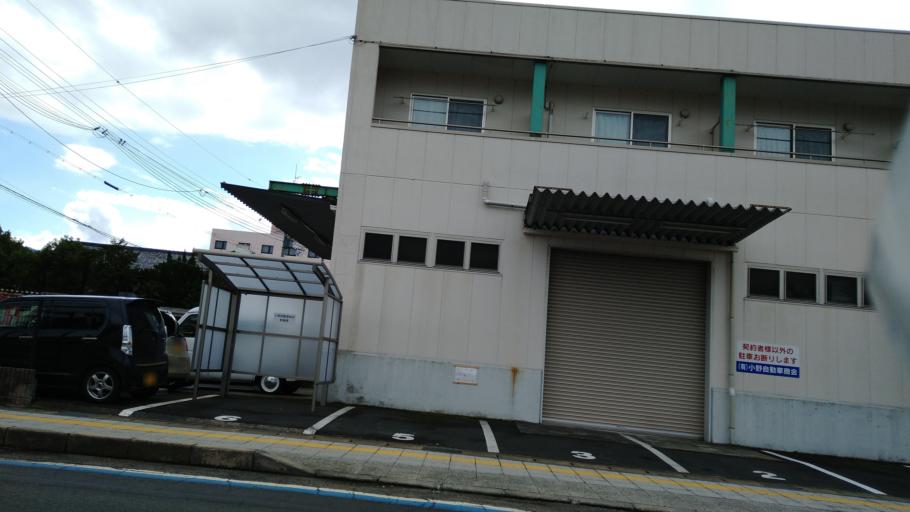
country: JP
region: Kyoto
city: Maizuru
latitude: 35.4768
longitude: 135.3925
